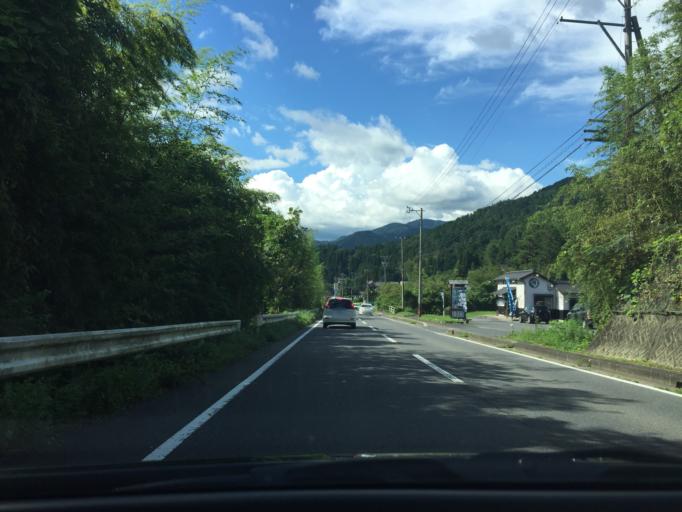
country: JP
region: Gifu
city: Nakatsugawa
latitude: 35.6582
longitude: 137.4322
